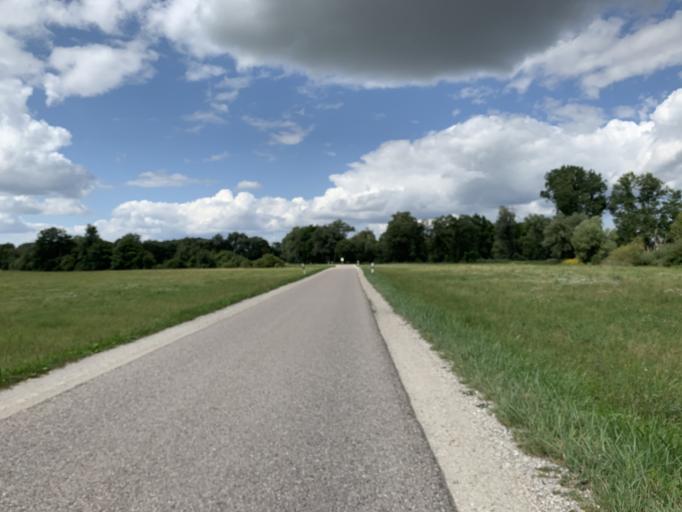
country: DE
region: Bavaria
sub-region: Upper Bavaria
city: Zolling
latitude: 48.4441
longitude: 11.7847
